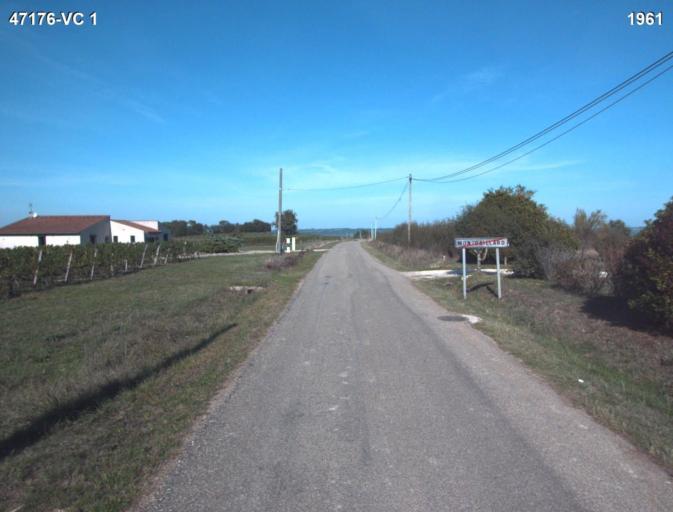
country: FR
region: Aquitaine
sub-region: Departement du Lot-et-Garonne
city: Vianne
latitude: 44.2101
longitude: 0.2951
